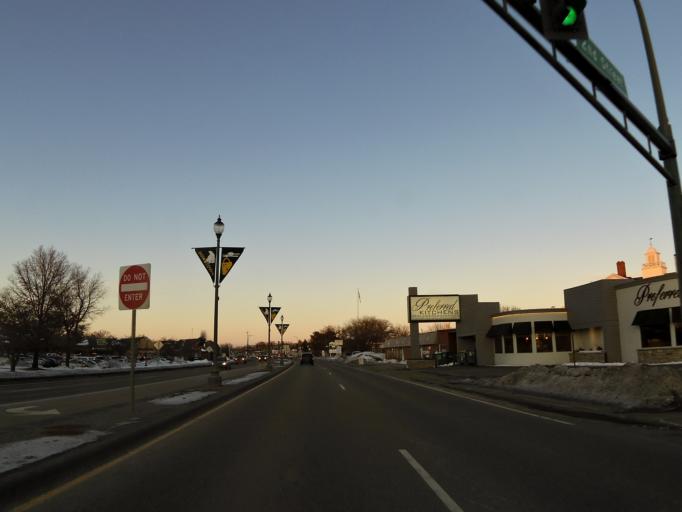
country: US
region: Minnesota
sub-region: Ramsey County
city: White Bear Lake
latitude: 45.0834
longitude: -93.0114
